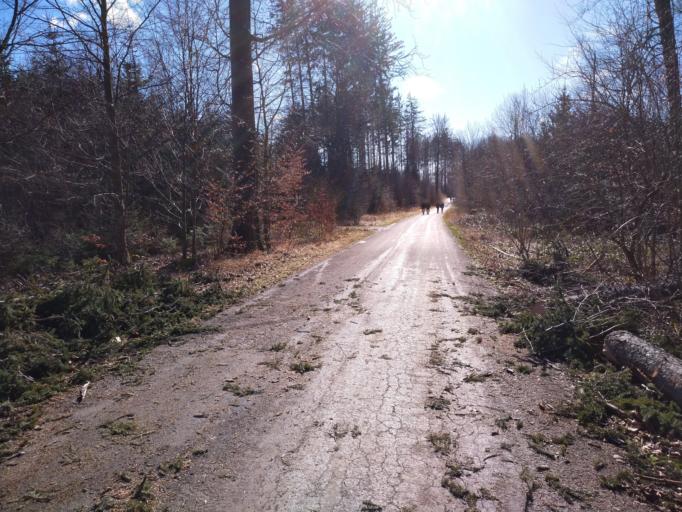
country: DE
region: Bavaria
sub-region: Swabia
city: Bad Worishofen
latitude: 47.9918
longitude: 10.5698
